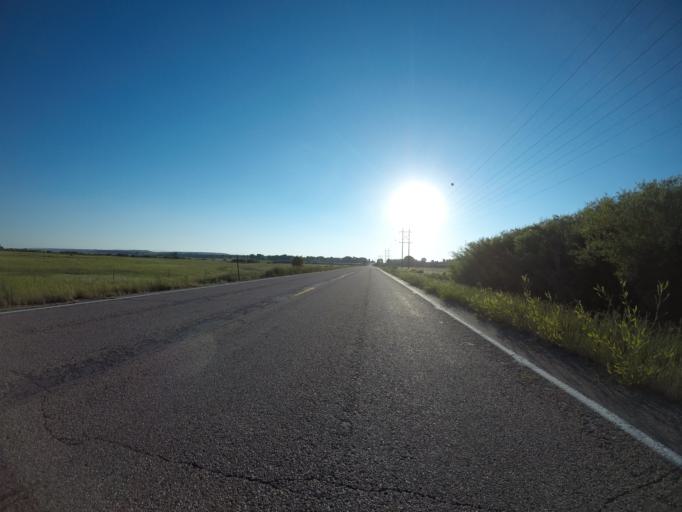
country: US
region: Wyoming
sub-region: Sublette County
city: Marbleton
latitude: 42.5728
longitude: -109.9427
